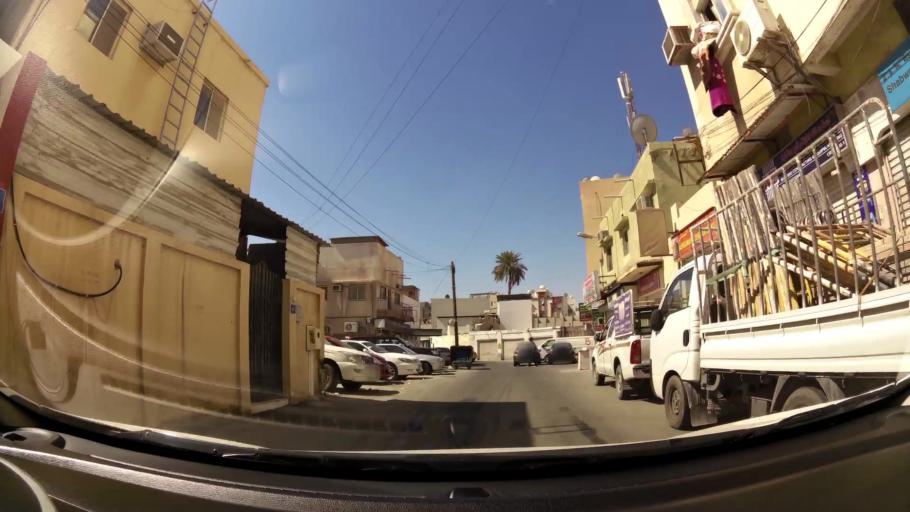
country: BH
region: Muharraq
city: Al Muharraq
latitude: 26.2557
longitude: 50.6162
